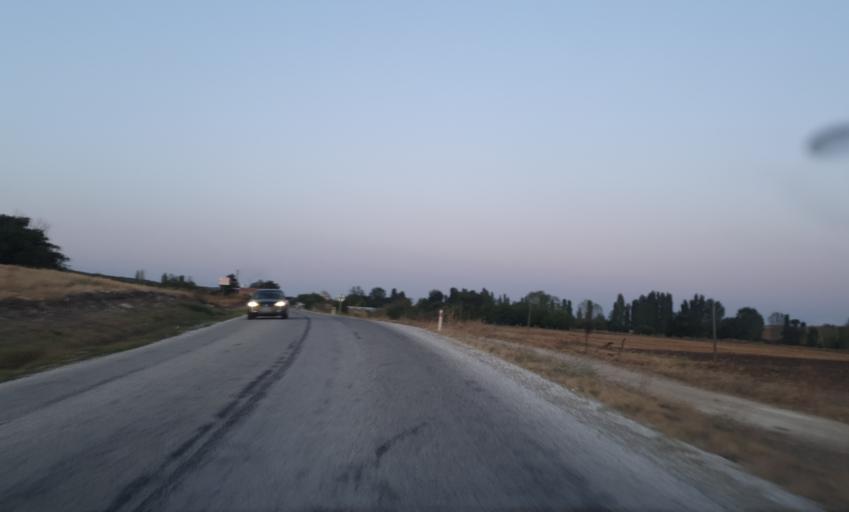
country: TR
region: Kirklareli
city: Pinarhisar
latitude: 41.6256
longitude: 27.5635
